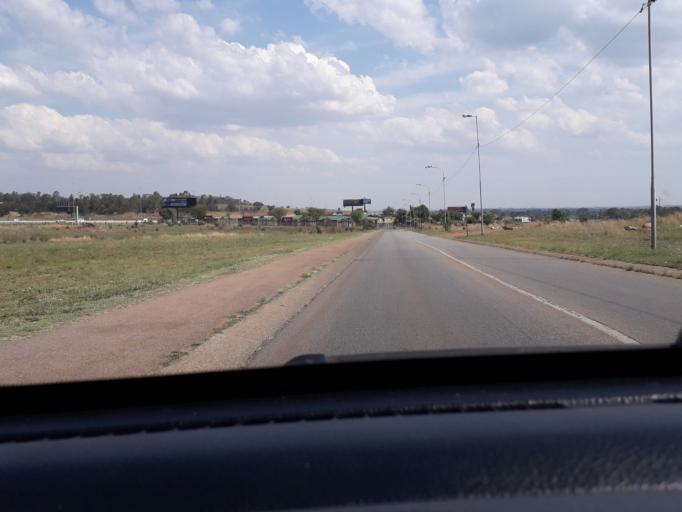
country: ZA
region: Gauteng
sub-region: City of Tshwane Metropolitan Municipality
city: Centurion
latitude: -25.8465
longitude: 28.2268
